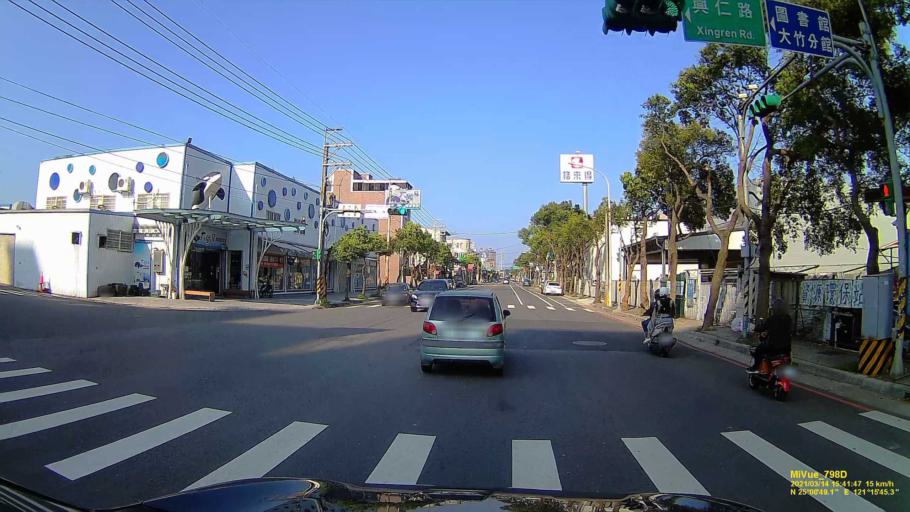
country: TW
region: Taiwan
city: Taoyuan City
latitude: 25.0138
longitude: 121.2627
